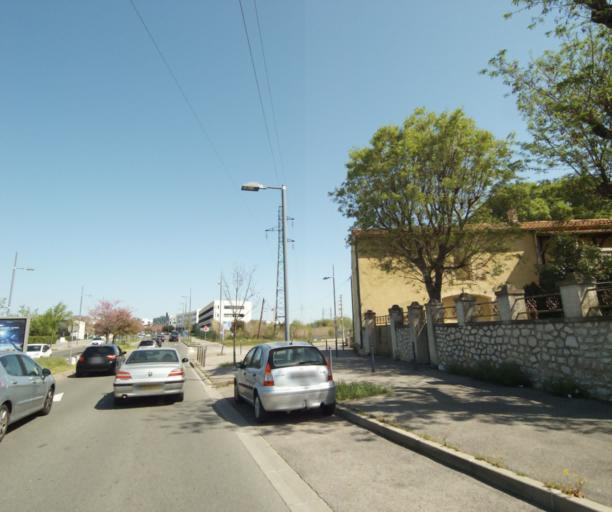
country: FR
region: Languedoc-Roussillon
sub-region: Departement de l'Herault
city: Castelnau-le-Lez
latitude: 43.6133
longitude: 3.9148
